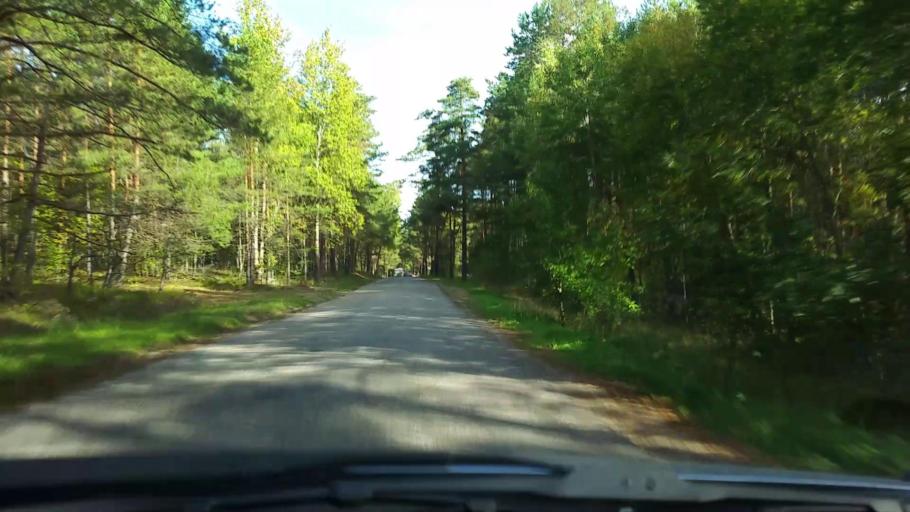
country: LV
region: Adazi
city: Adazi
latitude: 57.0978
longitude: 24.3719
